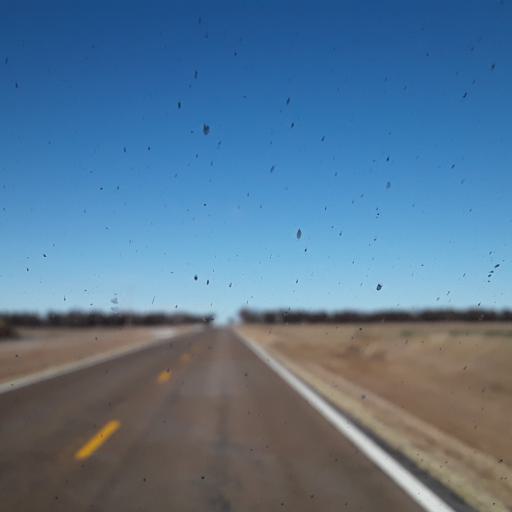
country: US
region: Kansas
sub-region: Mitchell County
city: Beloit
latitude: 39.3378
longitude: -98.1160
